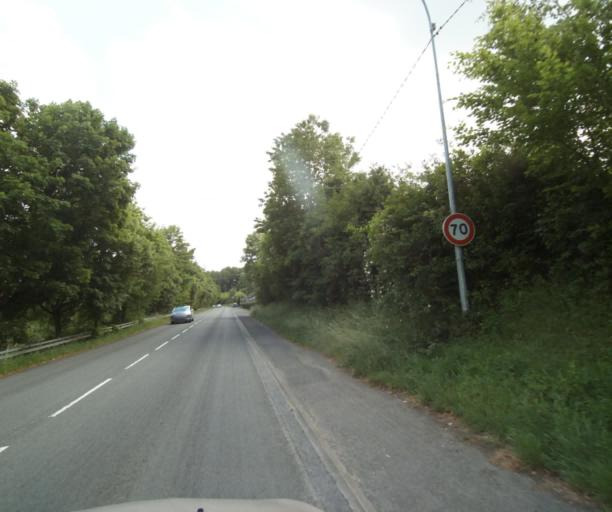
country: FR
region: Champagne-Ardenne
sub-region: Departement des Ardennes
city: Montcy-Notre-Dame
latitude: 49.7666
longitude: 4.7435
